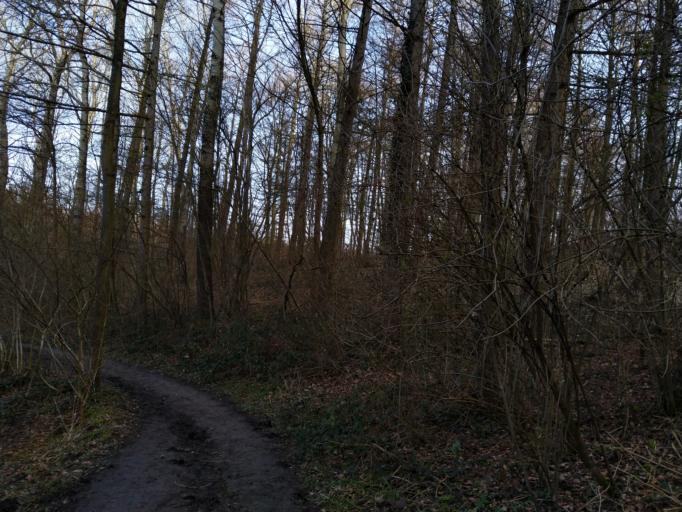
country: BE
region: Wallonia
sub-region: Province du Hainaut
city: Mons
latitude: 50.5032
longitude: 4.0220
